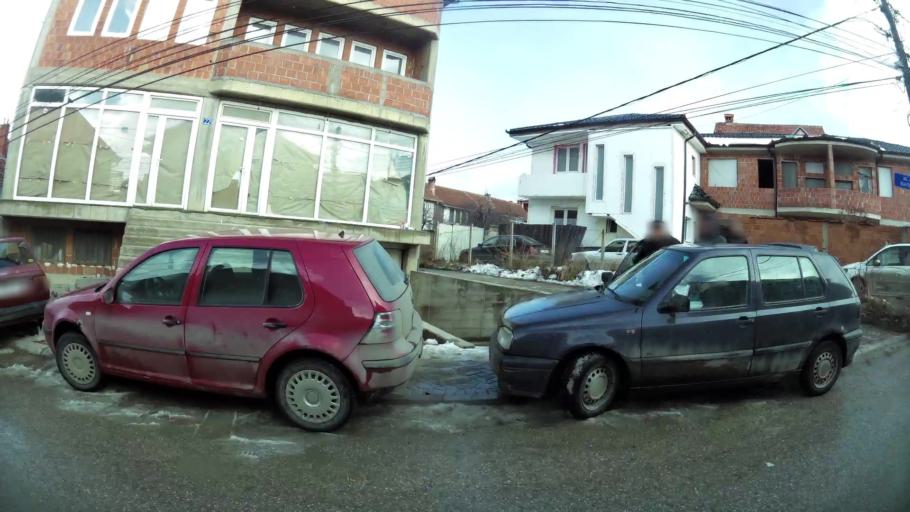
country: XK
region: Pristina
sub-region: Komuna e Prishtines
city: Pristina
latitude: 42.6845
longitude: 21.1546
